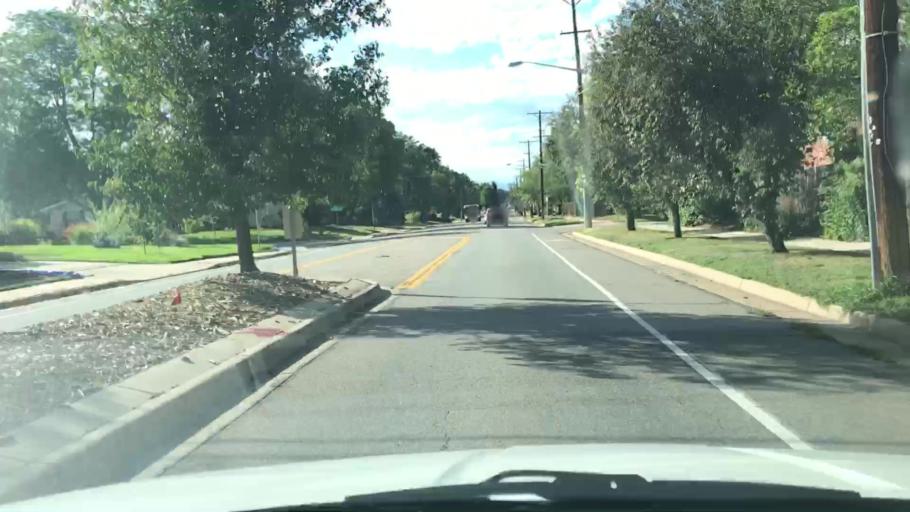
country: US
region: Colorado
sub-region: Arapahoe County
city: Cherry Hills Village
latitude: 39.6485
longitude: -104.9258
